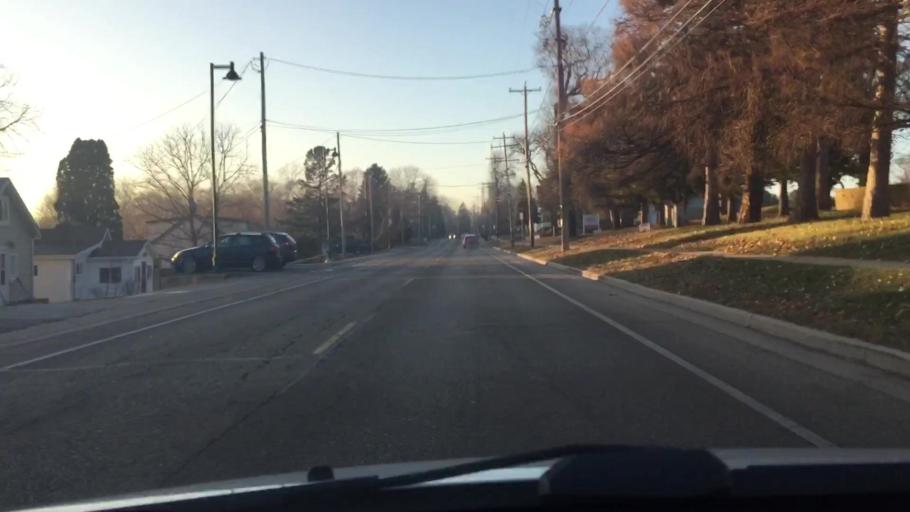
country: US
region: Wisconsin
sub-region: Waukesha County
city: Pewaukee
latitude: 43.0866
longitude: -88.2681
